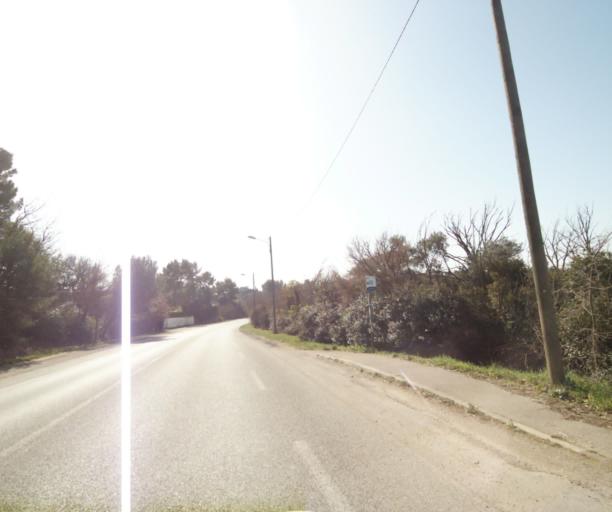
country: FR
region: Provence-Alpes-Cote d'Azur
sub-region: Departement des Bouches-du-Rhone
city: Aix-en-Provence
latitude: 43.4961
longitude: 5.4334
